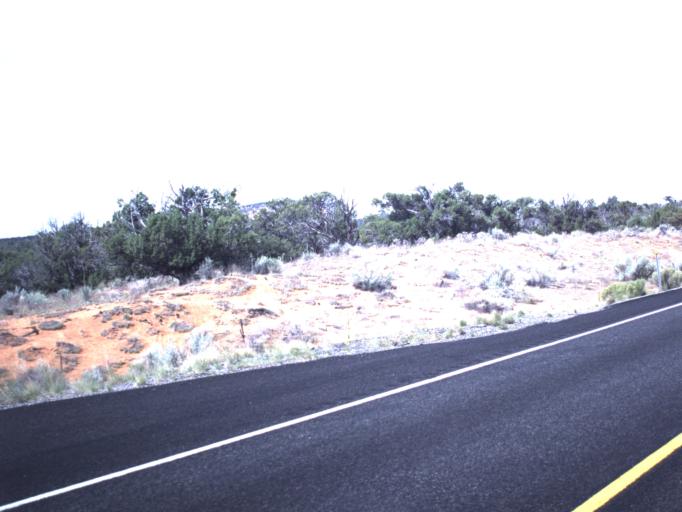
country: US
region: Utah
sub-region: Kane County
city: Kanab
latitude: 37.1628
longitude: -112.5933
